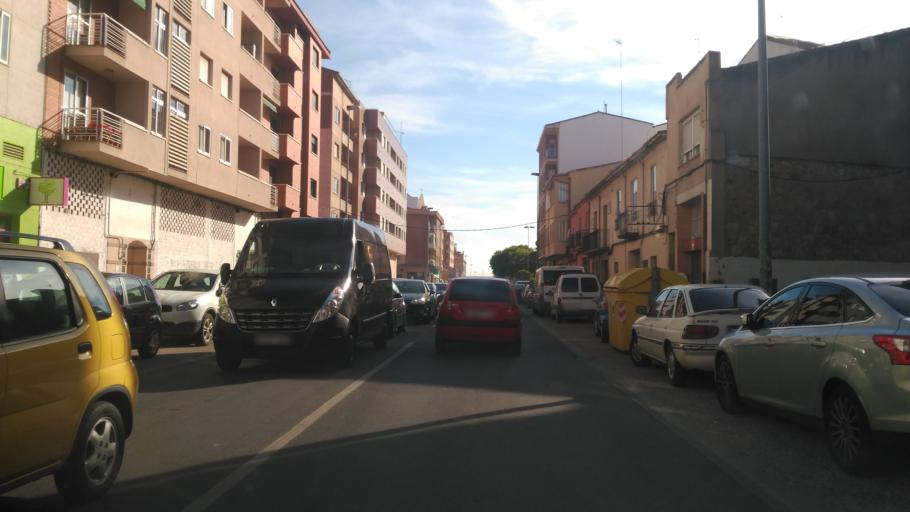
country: ES
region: Castille and Leon
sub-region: Provincia de Zamora
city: Zamora
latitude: 41.5058
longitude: -5.7506
